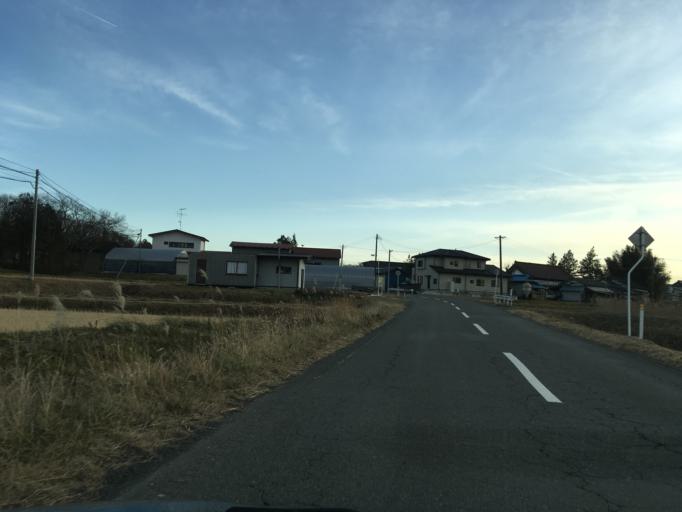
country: JP
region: Miyagi
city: Kogota
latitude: 38.6839
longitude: 141.0959
